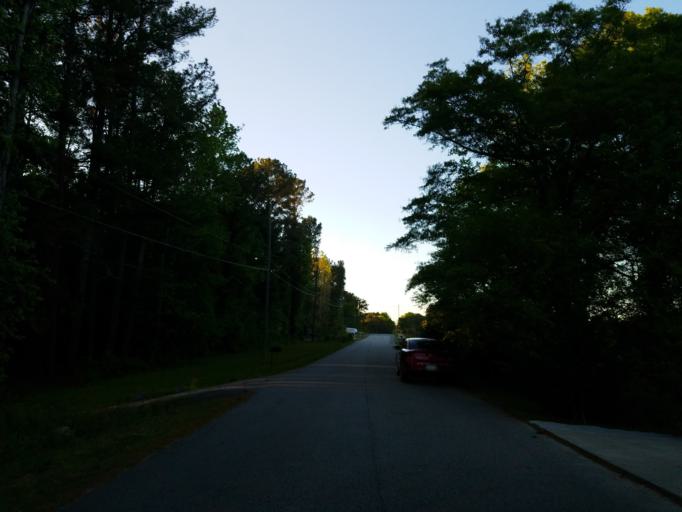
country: US
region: Georgia
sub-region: Cobb County
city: Powder Springs
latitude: 33.8952
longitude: -84.6344
